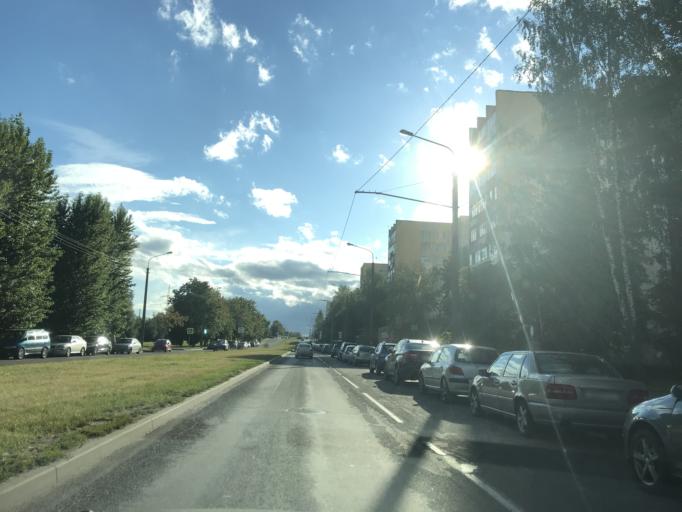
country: BY
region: Minsk
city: Minsk
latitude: 53.9498
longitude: 27.6122
